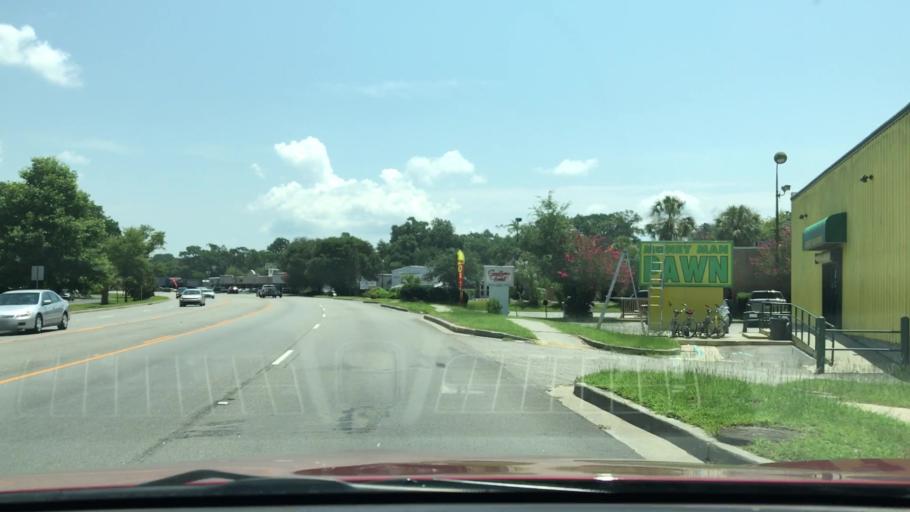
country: US
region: South Carolina
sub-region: Berkeley County
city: Hanahan
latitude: 32.8559
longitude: -80.0416
